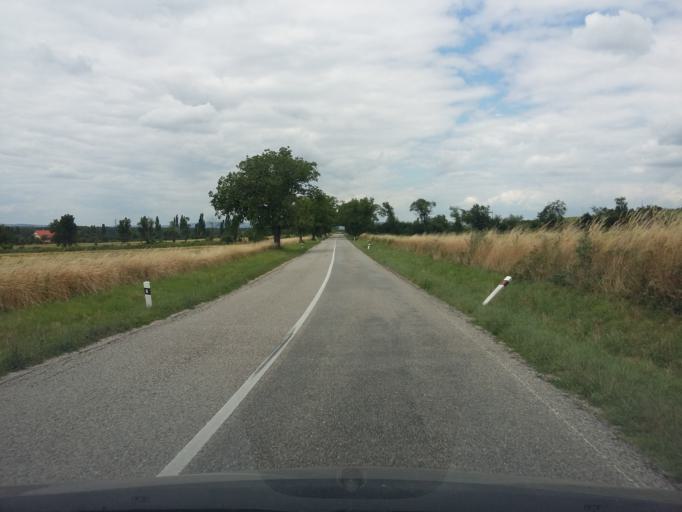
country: SK
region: Trnavsky
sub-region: Okres Senica
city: Senica
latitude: 48.5752
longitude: 17.3520
